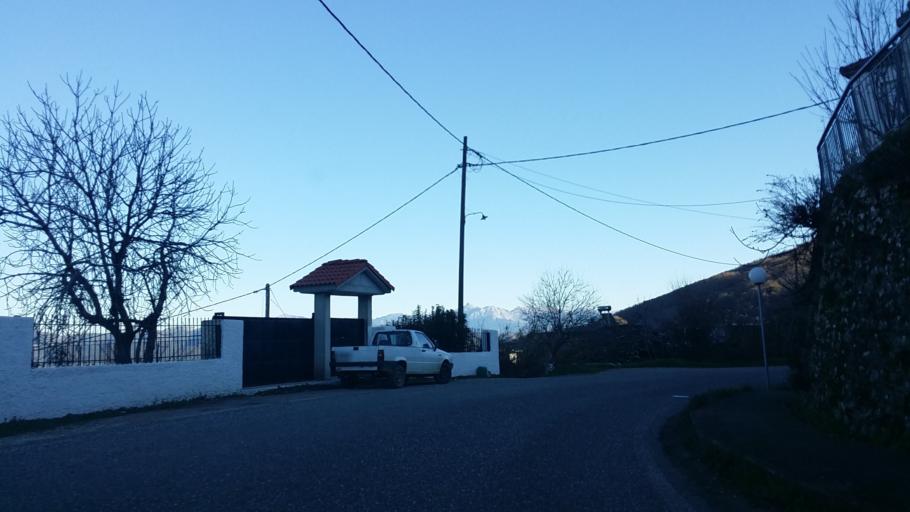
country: GR
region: West Greece
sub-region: Nomos Aitolias kai Akarnanias
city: Sardinia
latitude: 38.8694
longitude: 21.2855
